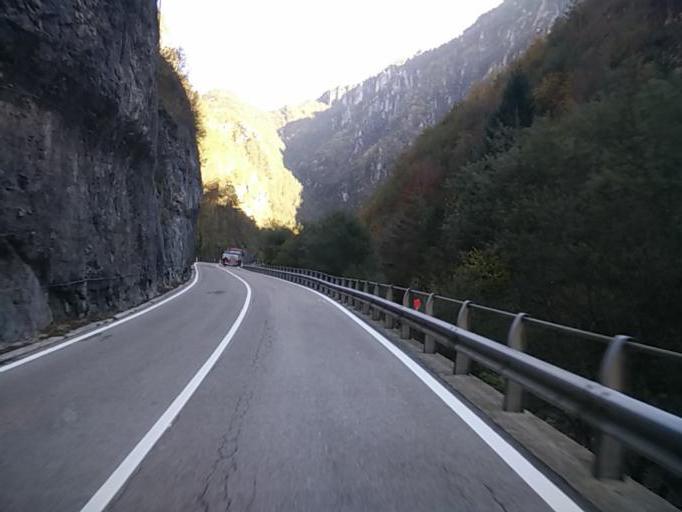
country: IT
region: Trentino-Alto Adige
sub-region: Provincia di Trento
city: Storo
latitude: 45.8441
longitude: 10.6129
